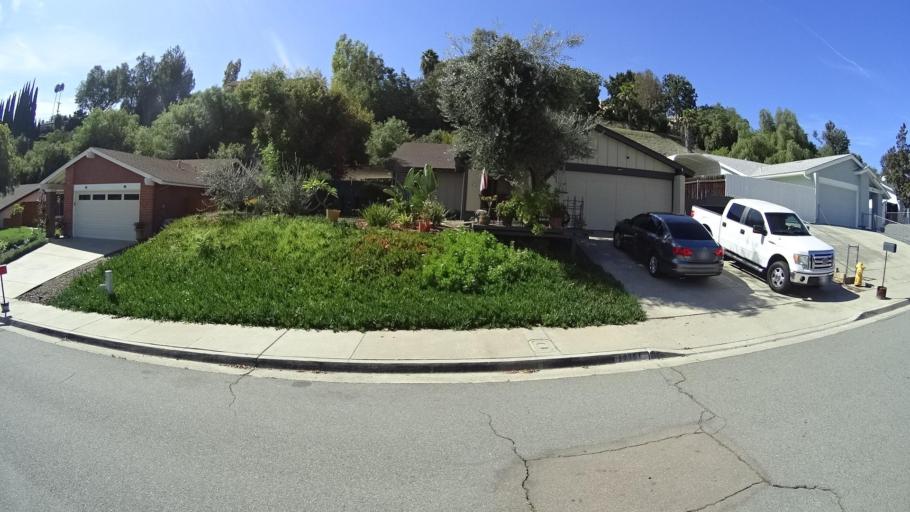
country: US
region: California
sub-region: San Diego County
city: Casa de Oro-Mount Helix
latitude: 32.7520
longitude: -116.9689
